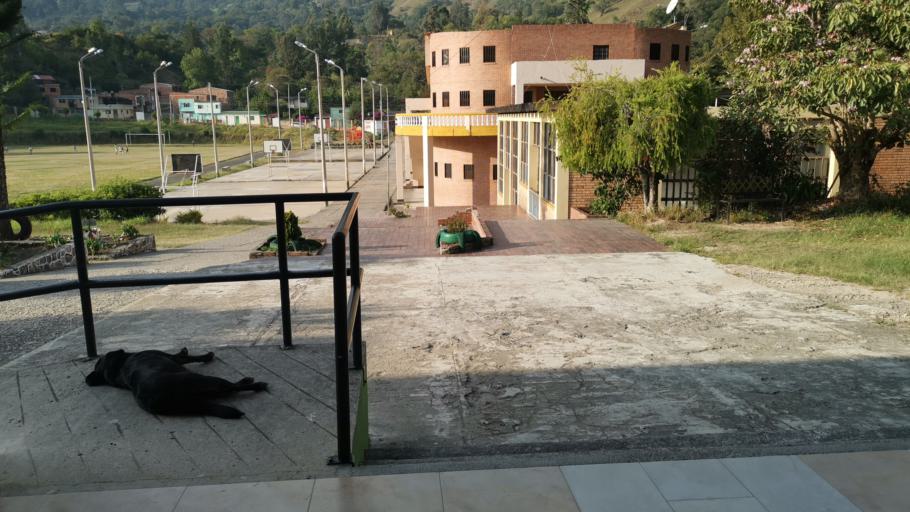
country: CO
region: Boyaca
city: San Mateo
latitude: 6.3998
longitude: -72.5529
